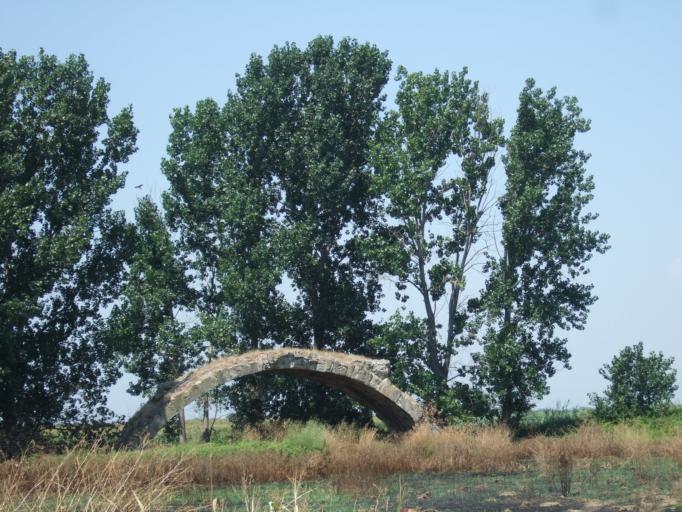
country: GR
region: Central Macedonia
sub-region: Nomos Imathias
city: Kleidi
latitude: 40.5734
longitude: 22.6235
